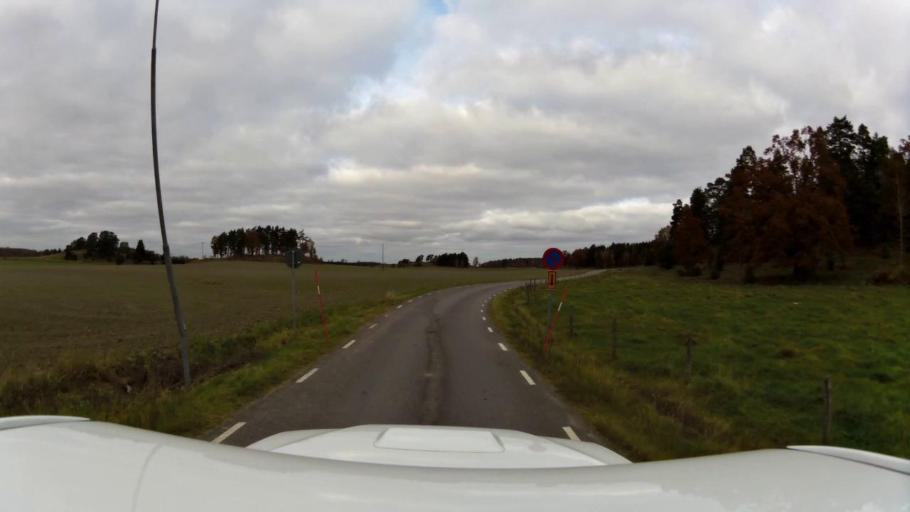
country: SE
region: OEstergoetland
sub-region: Linkopings Kommun
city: Linghem
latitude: 58.3785
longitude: 15.8211
